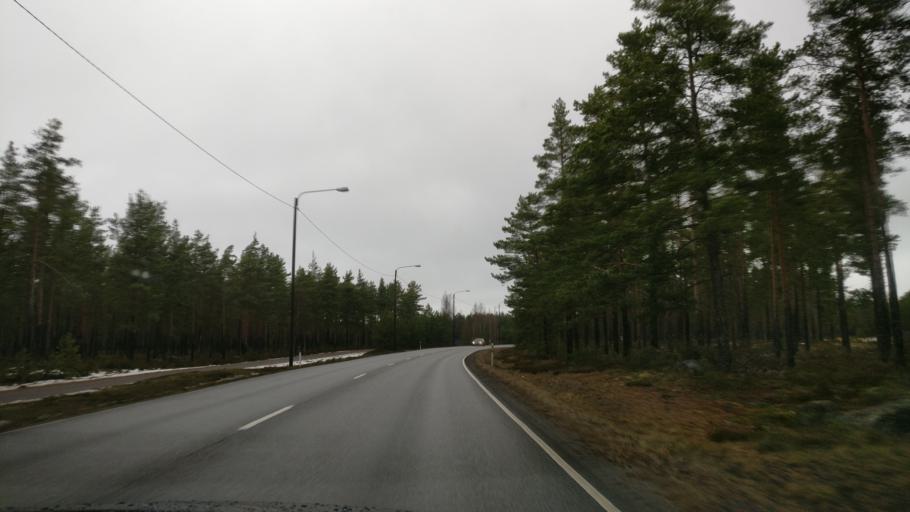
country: FI
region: Uusimaa
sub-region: Raaseporin
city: Hanko
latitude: 59.8477
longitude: 23.0056
